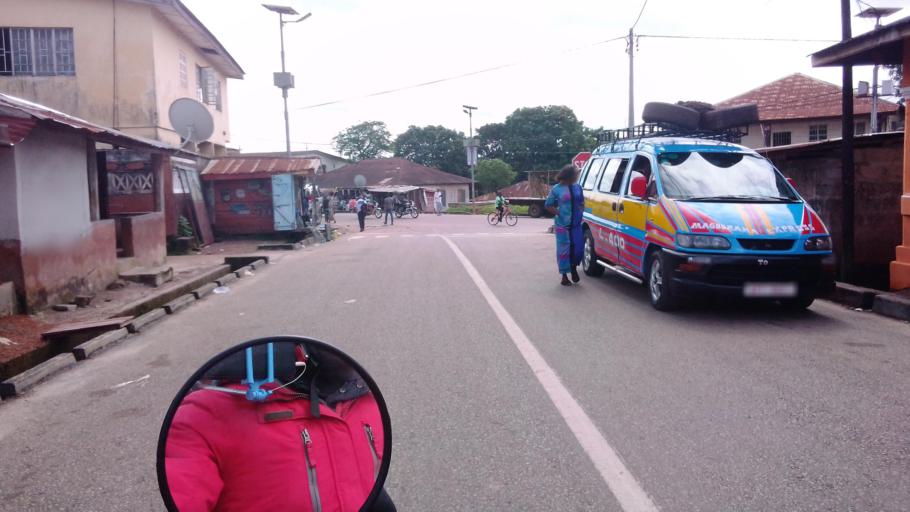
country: SL
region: Northern Province
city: Makeni
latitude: 8.8871
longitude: -12.0455
